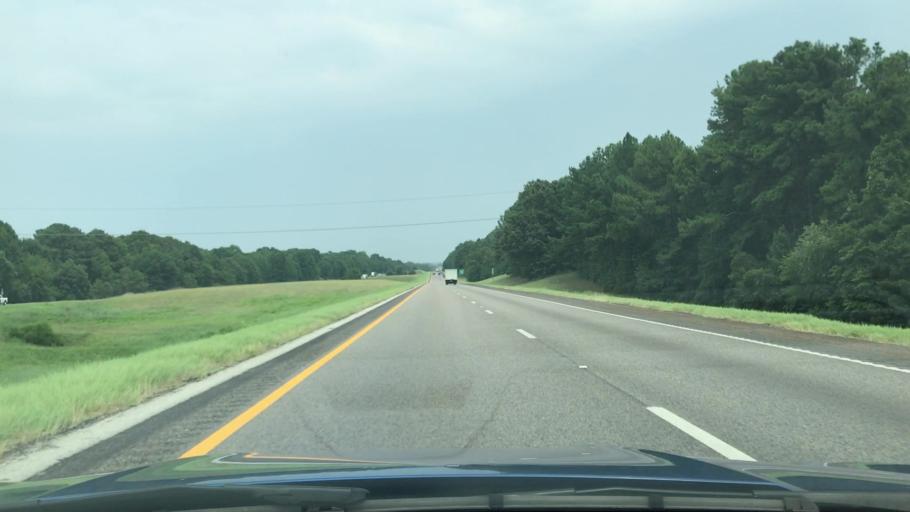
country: US
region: Texas
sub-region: Smith County
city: Tyler
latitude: 32.4521
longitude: -95.2578
